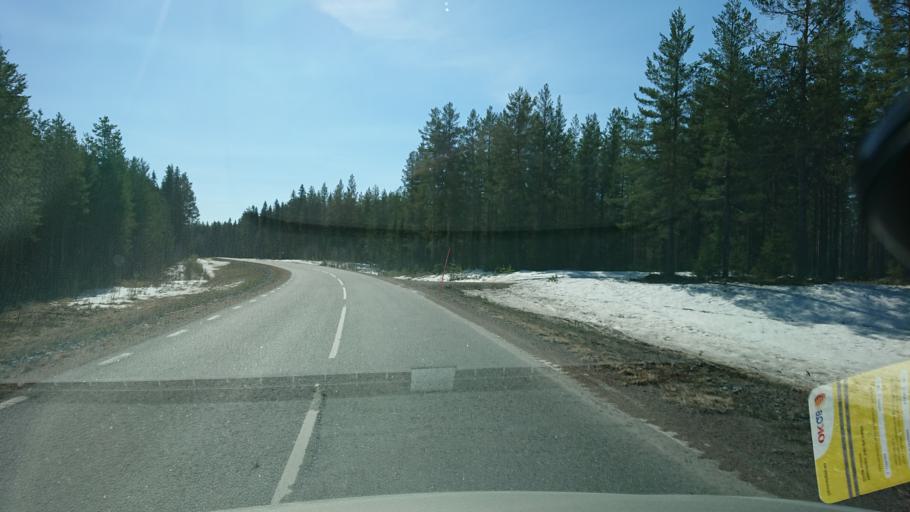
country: SE
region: Vaesternorrland
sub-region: Solleftea Kommun
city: As
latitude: 63.6711
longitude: 16.4294
